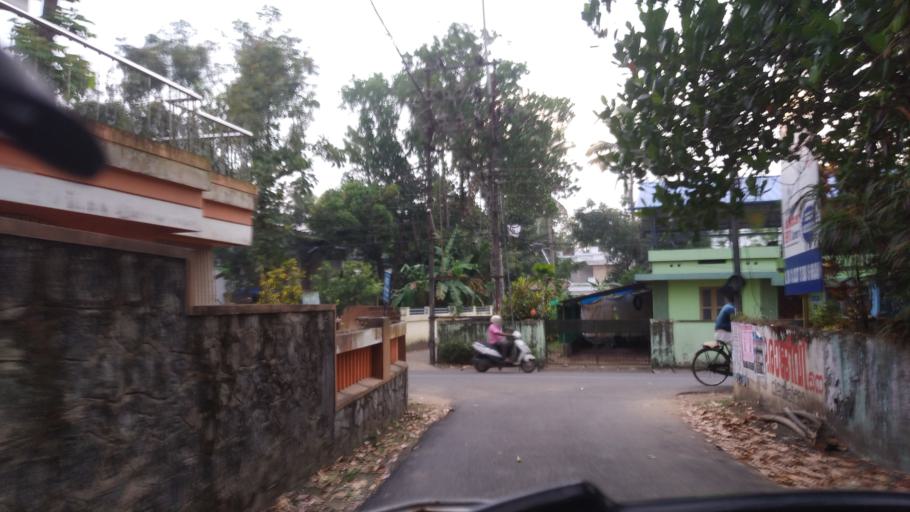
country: IN
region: Kerala
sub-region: Thrissur District
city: Kodungallur
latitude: 10.1368
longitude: 76.2204
